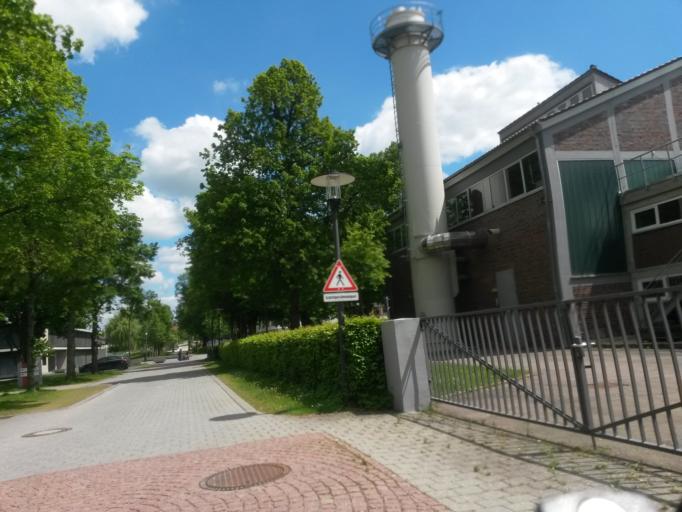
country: DE
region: Baden-Wuerttemberg
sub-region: Tuebingen Region
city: Bad Schussenried
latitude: 48.0094
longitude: 9.6577
